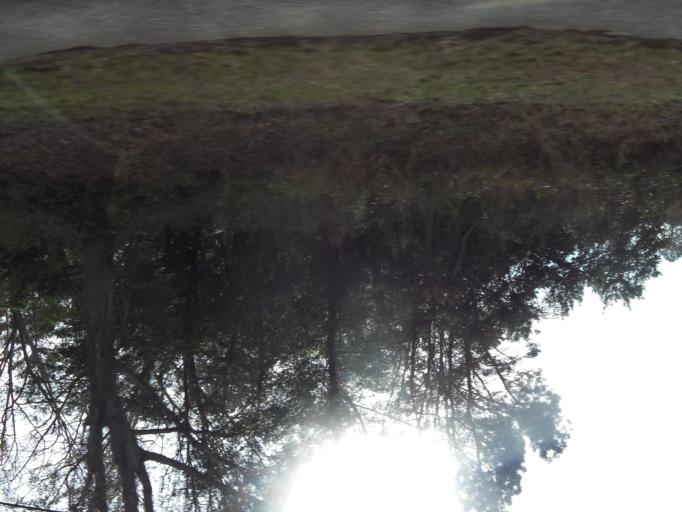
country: US
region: Alabama
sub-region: Houston County
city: Cowarts
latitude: 31.2028
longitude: -85.3451
